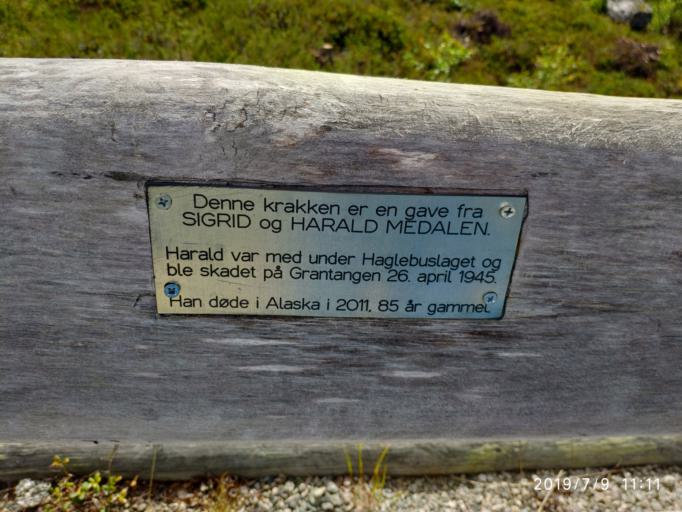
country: NO
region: Buskerud
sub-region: Nore og Uvdal
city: Rodberg
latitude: 60.3341
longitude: 9.1792
